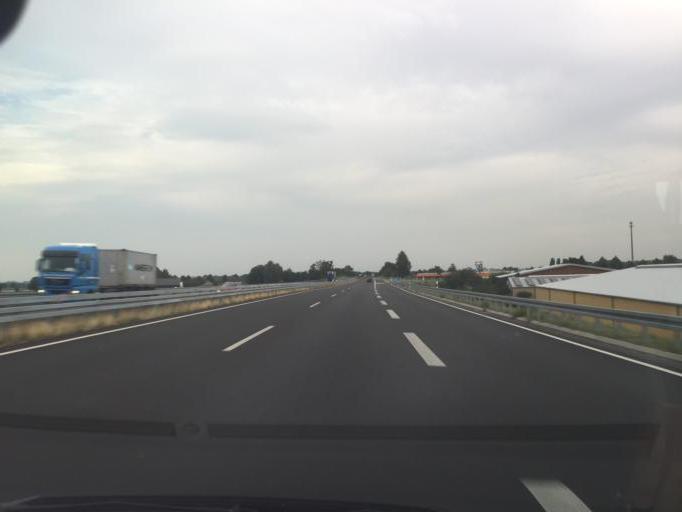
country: NL
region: Limburg
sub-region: Gemeente Venlo
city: Venlo
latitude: 51.3324
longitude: 6.2063
